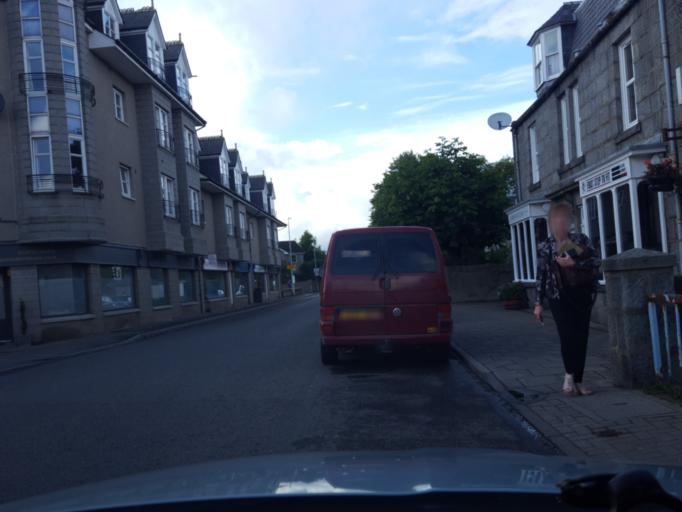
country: GB
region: Scotland
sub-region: Aberdeenshire
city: Alford
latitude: 57.2322
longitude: -2.7024
